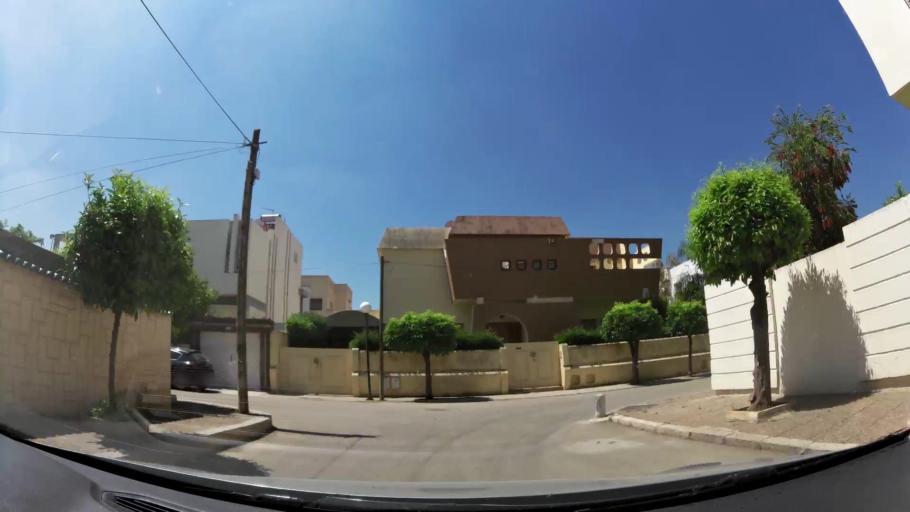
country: MA
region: Fes-Boulemane
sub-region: Fes
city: Fes
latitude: 34.0288
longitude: -5.0116
